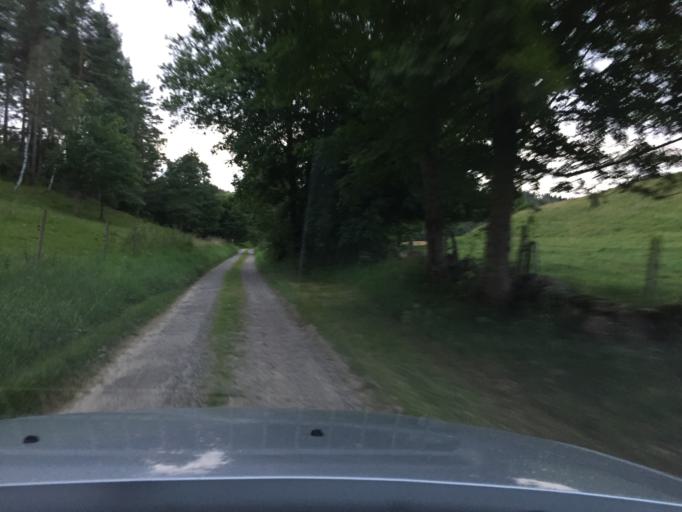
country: SE
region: Skane
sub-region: Kristianstads Kommun
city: Degeberga
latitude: 55.7248
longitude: 14.1279
